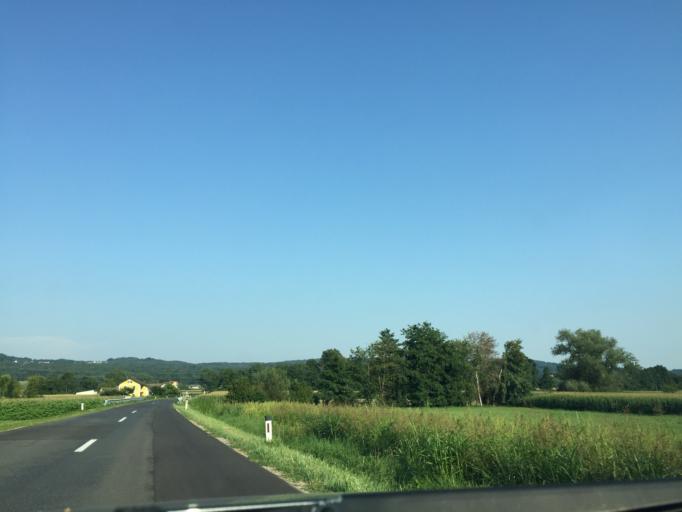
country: AT
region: Styria
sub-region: Politischer Bezirk Suedoststeiermark
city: Straden
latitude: 46.8102
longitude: 15.8813
